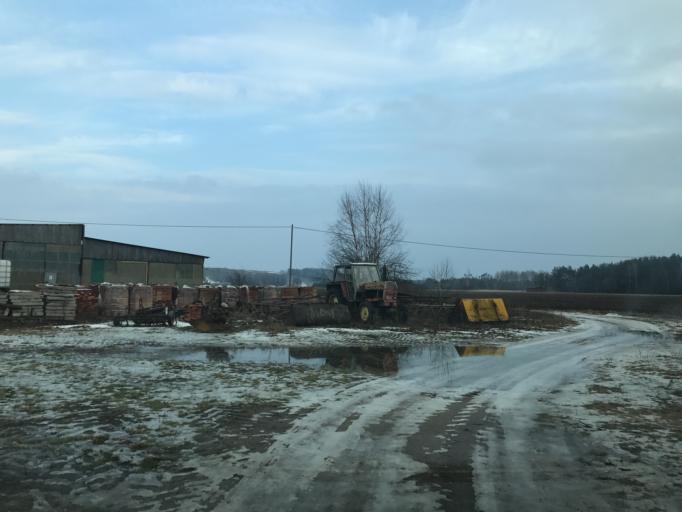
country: PL
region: Kujawsko-Pomorskie
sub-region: Powiat brodnicki
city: Brzozie
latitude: 53.2984
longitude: 19.5582
